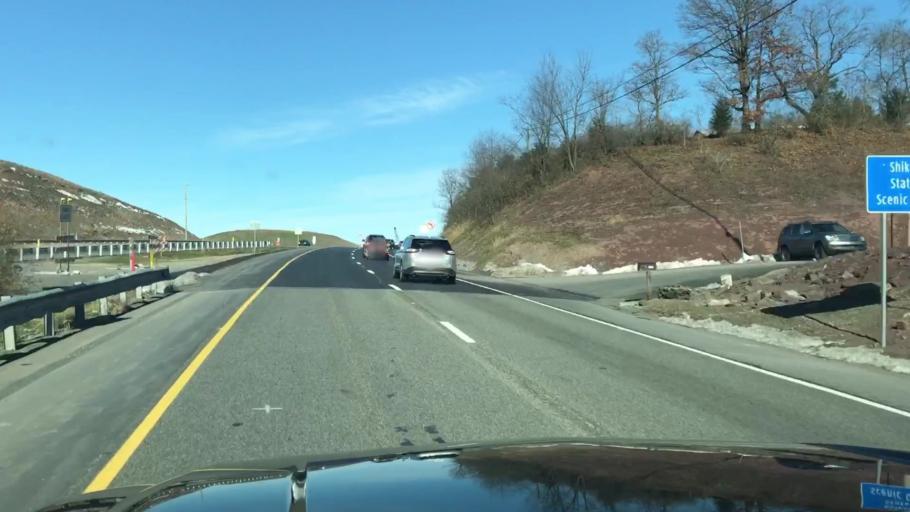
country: US
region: Pennsylvania
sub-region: Snyder County
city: Shamokin Dam
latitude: 40.8837
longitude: -76.8412
